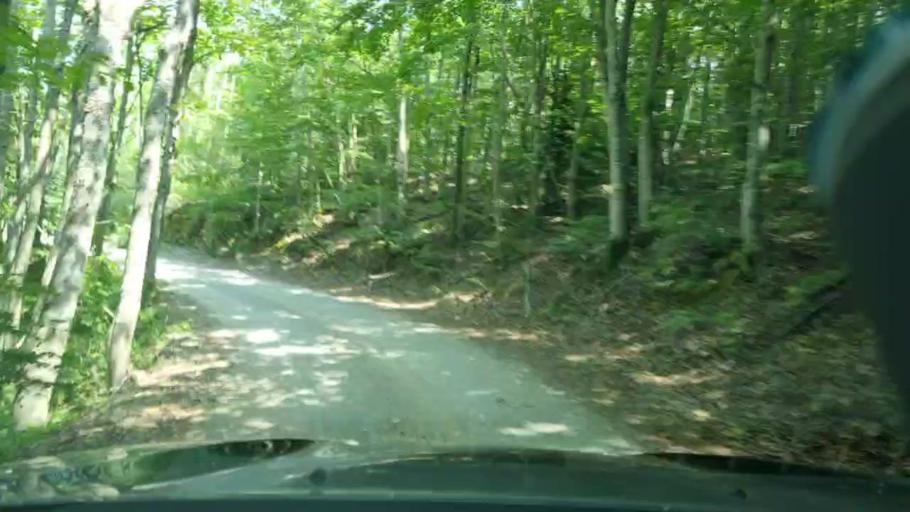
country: BA
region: Federation of Bosnia and Herzegovina
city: Bosansko Grahovo
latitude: 44.3261
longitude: 16.2370
